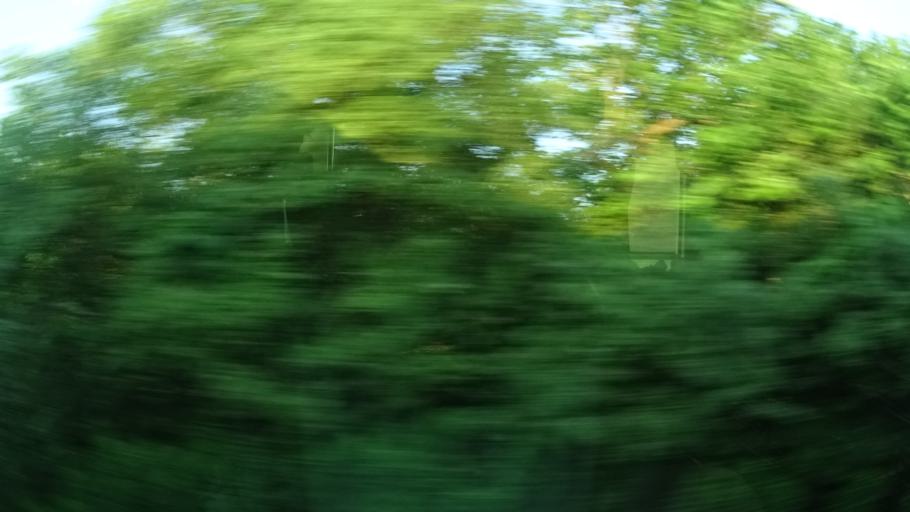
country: JP
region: Ibaraki
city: Tomobe
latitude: 36.2837
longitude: 140.2778
